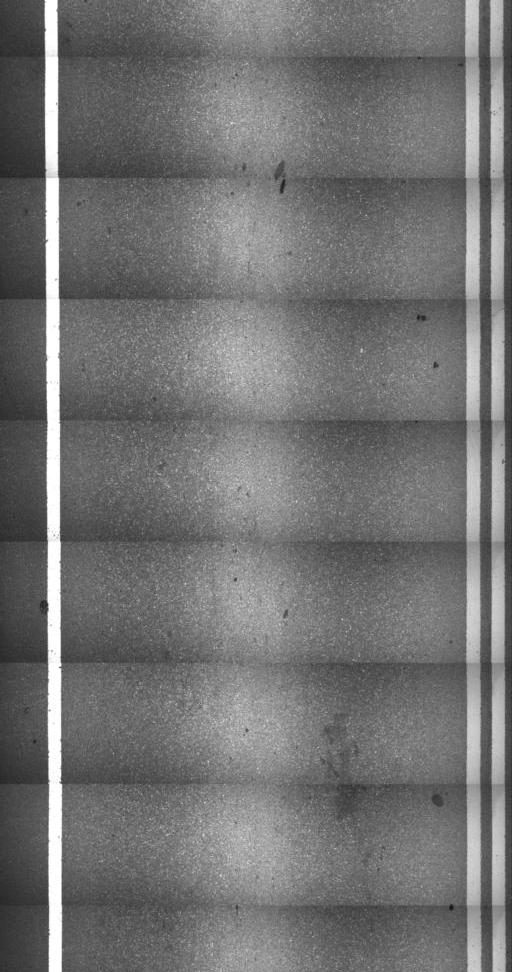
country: US
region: Vermont
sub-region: Washington County
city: Waterbury
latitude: 44.3196
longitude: -72.7593
